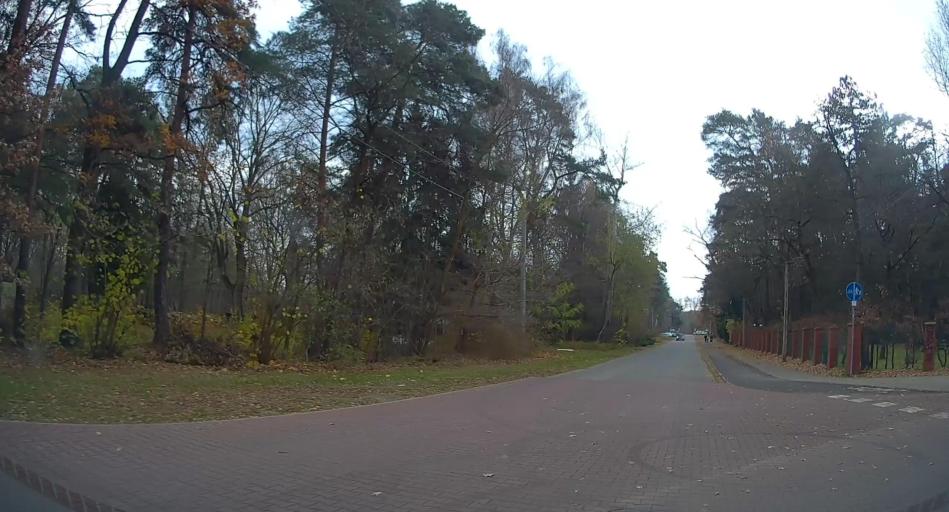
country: PL
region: Masovian Voivodeship
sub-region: Powiat piaseczynski
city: Zabieniec
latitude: 52.0537
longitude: 21.0221
